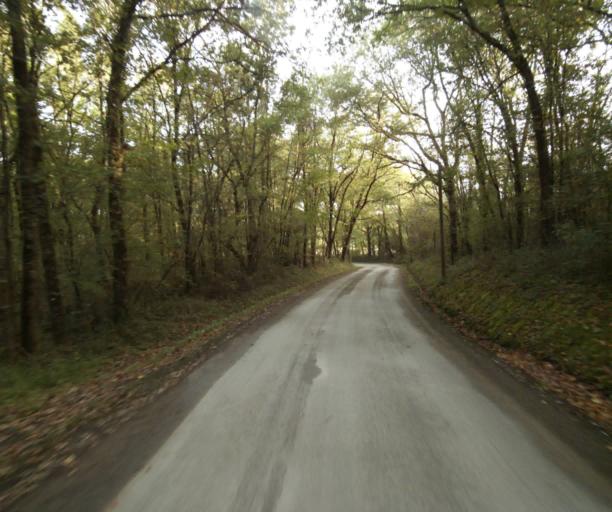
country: FR
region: Midi-Pyrenees
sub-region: Departement de la Haute-Garonne
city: Villemur-sur-Tarn
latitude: 43.9212
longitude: 1.5058
